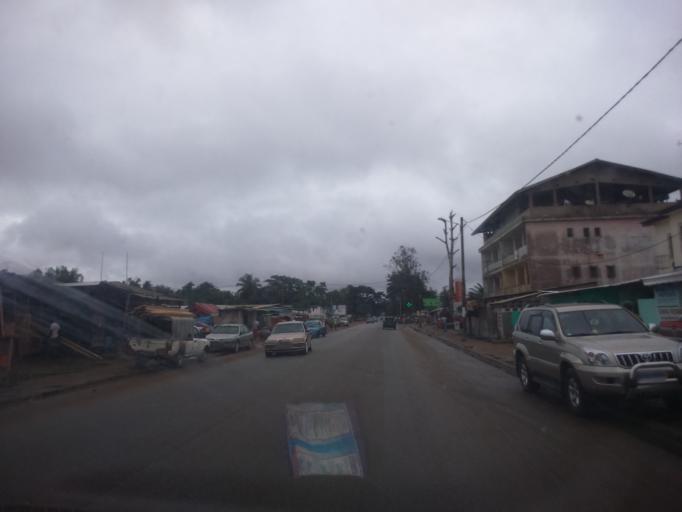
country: CI
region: Sud-Comoe
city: Bonoua
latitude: 5.2730
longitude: -3.5918
